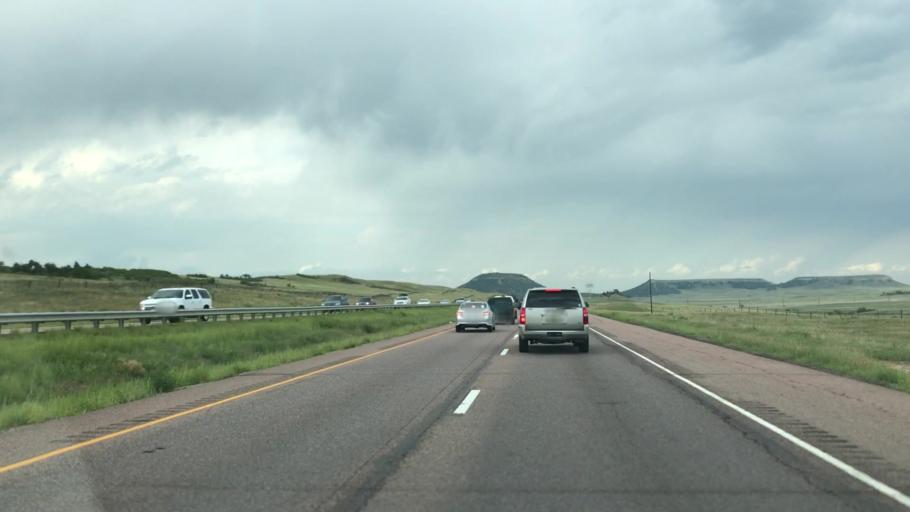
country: US
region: Colorado
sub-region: El Paso County
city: Woodmoor
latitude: 39.1536
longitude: -104.8576
